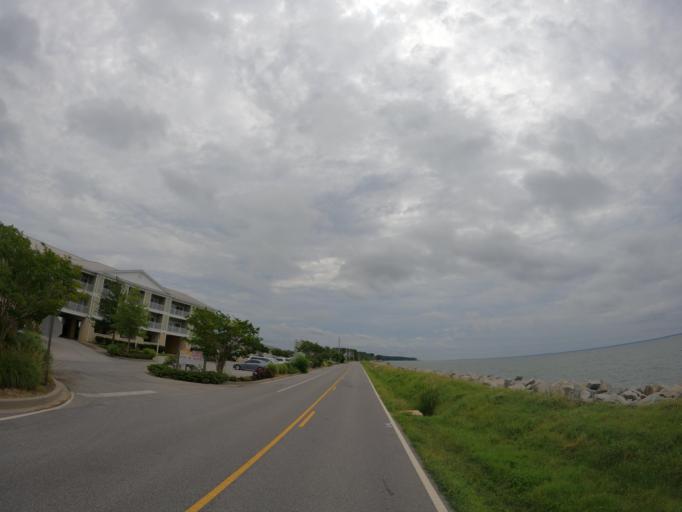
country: US
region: Maryland
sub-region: Saint Mary's County
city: Lexington Park
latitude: 38.1309
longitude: -76.4984
